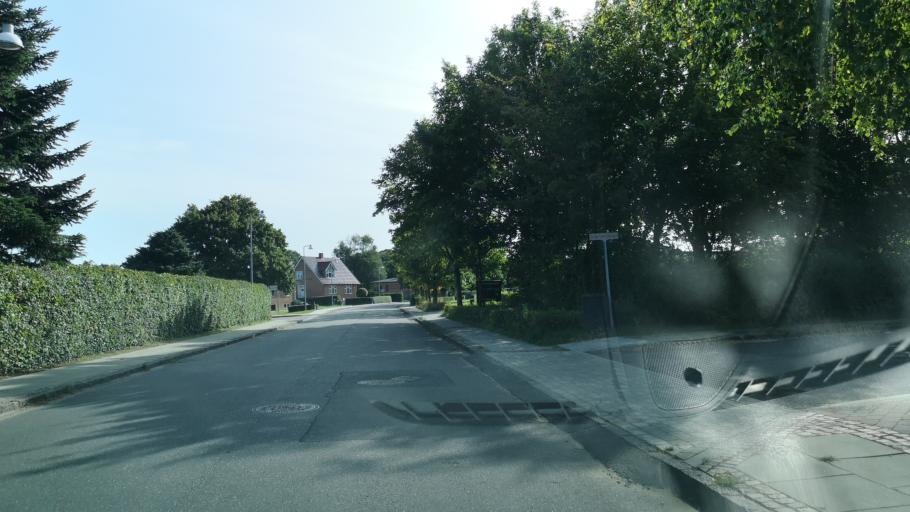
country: DK
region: Central Jutland
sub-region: Ikast-Brande Kommune
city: Ikast
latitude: 56.1475
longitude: 9.1503
